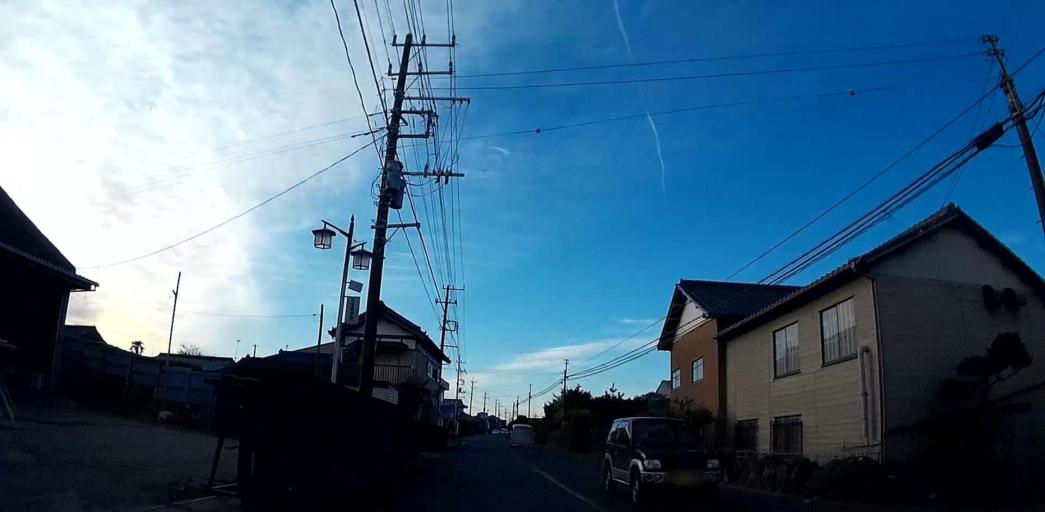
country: JP
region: Chiba
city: Omigawa
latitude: 35.8373
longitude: 140.6786
